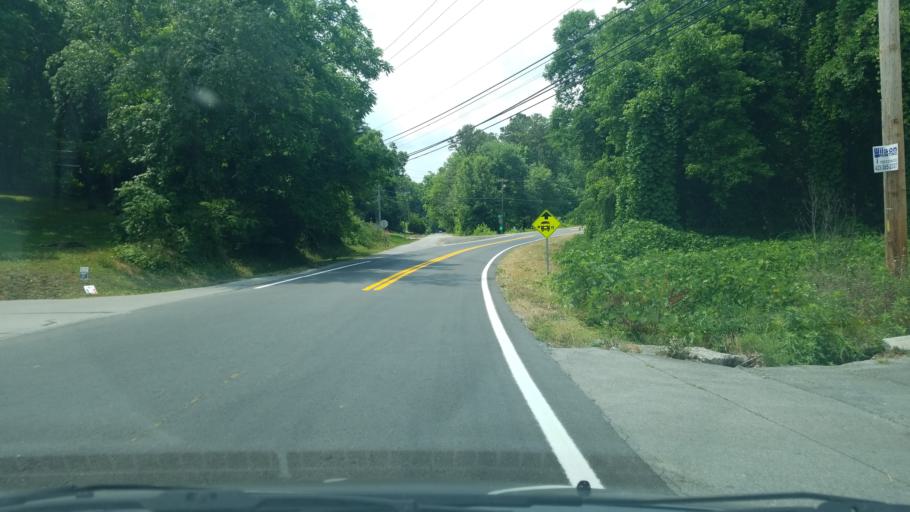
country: US
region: Tennessee
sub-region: Hamilton County
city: Lakesite
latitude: 35.2063
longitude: -85.1363
